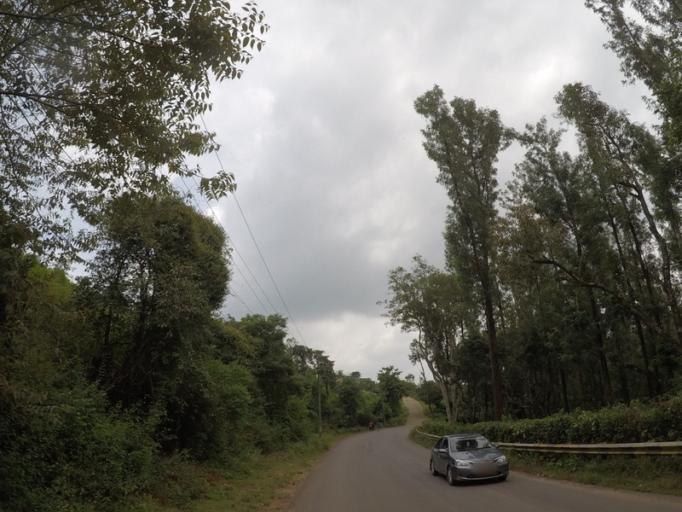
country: IN
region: Karnataka
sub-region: Chikmagalur
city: Chikmagalur
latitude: 13.3695
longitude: 75.7461
